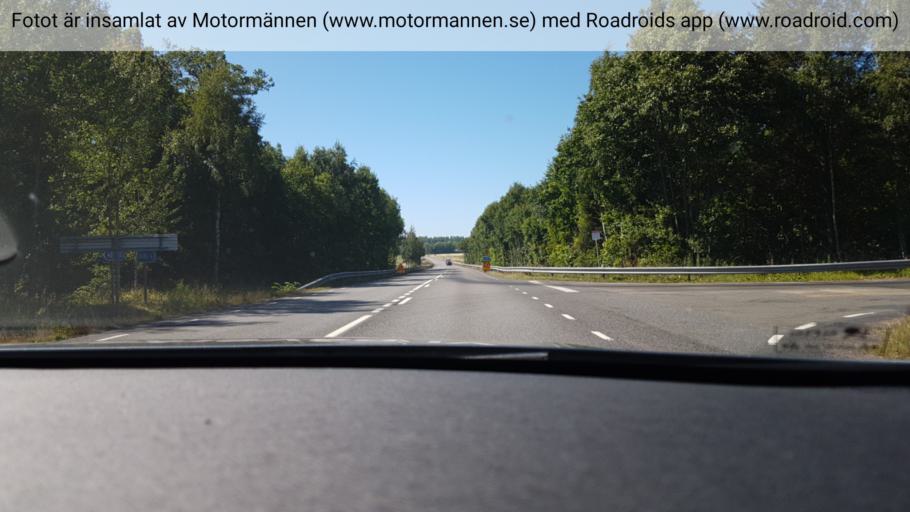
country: SE
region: Joenkoeping
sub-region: Habo Kommun
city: Habo
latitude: 57.9423
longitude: 14.0995
